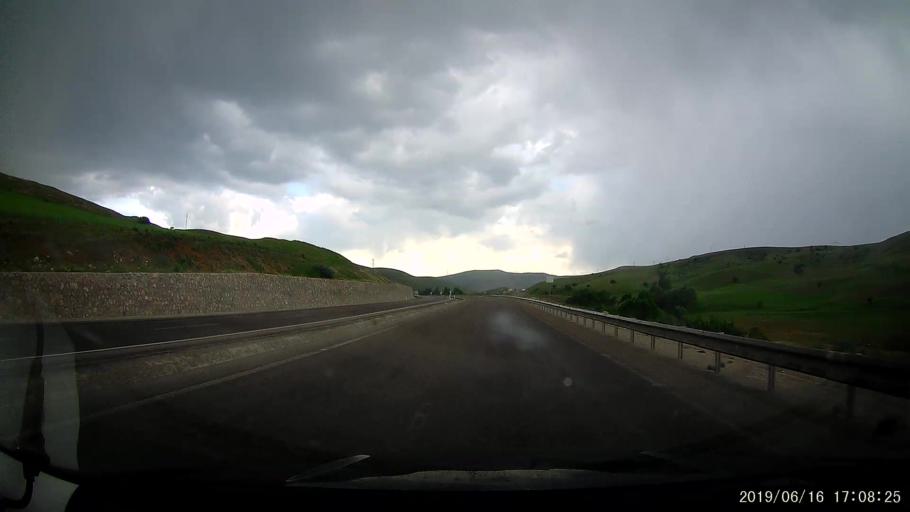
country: TR
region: Erzurum
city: Askale
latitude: 39.9093
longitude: 40.6613
